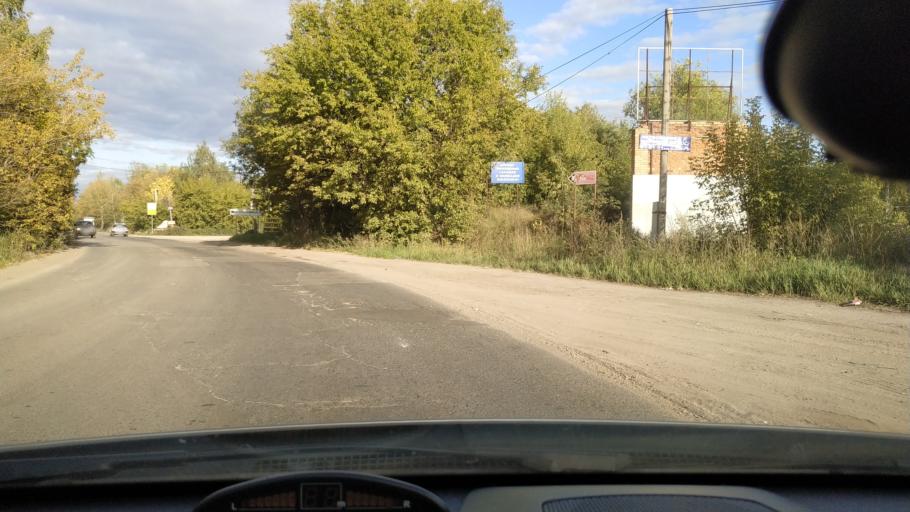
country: RU
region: Rjazan
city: Polyany
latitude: 54.5810
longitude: 39.8225
